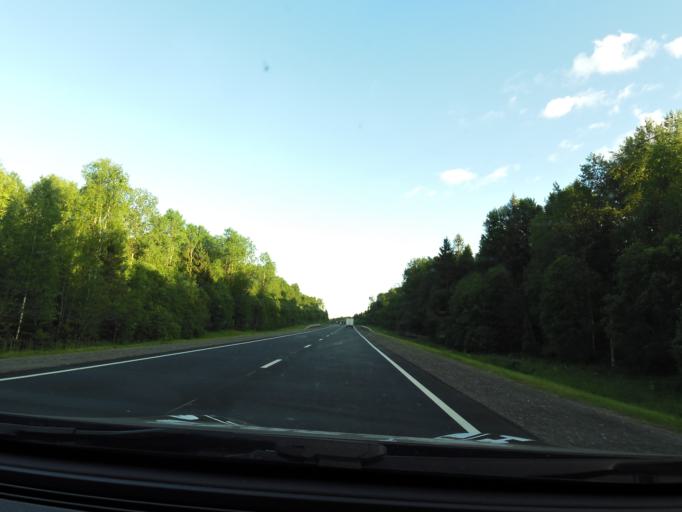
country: RU
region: Vologda
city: Gryazovets
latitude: 58.9240
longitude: 40.1763
